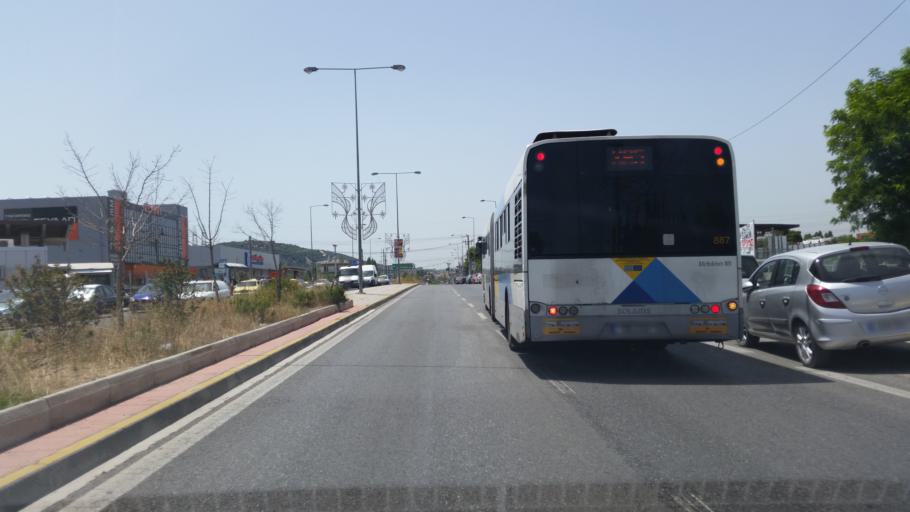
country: GR
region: Attica
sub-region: Nomarchia Anatolikis Attikis
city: Pallini
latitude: 38.0054
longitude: 23.8705
